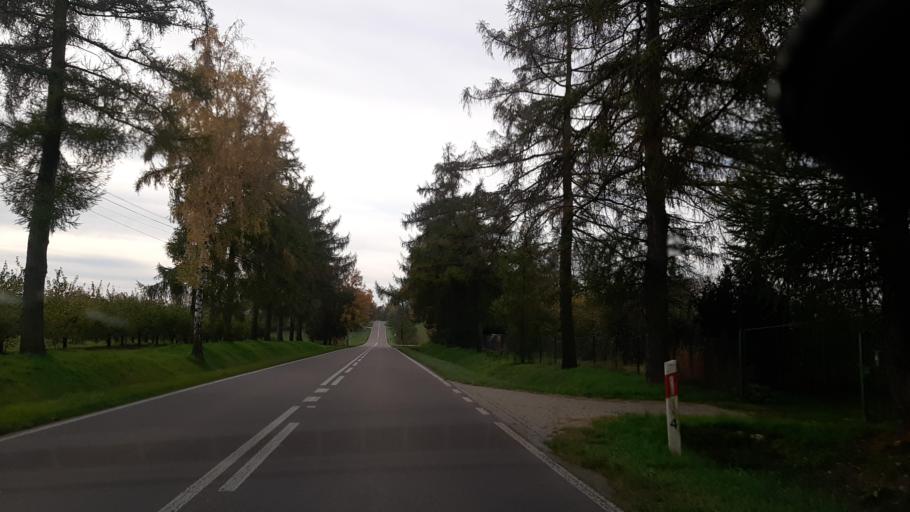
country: PL
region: Lublin Voivodeship
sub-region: Powiat pulawski
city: Markuszow
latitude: 51.3284
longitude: 22.2439
